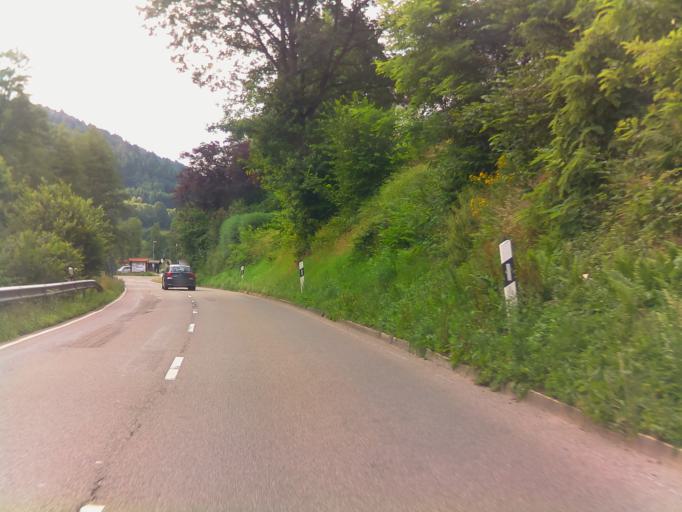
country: DE
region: Baden-Wuerttemberg
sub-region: Karlsruhe Region
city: Schonau
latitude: 49.4409
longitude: 8.8103
